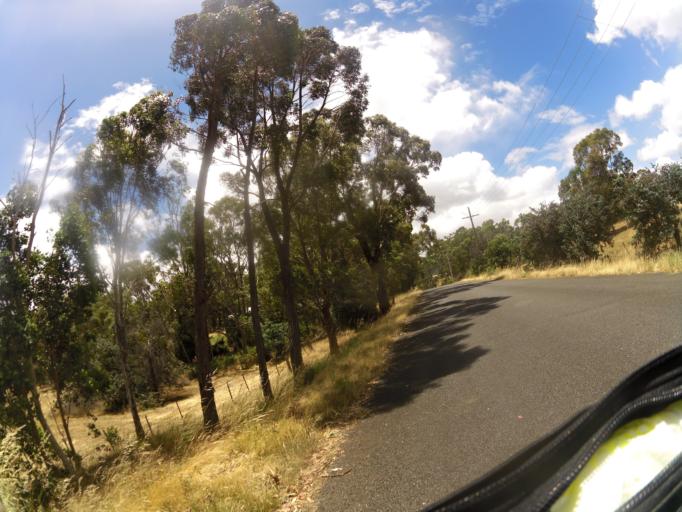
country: AU
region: Victoria
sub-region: Mount Alexander
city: Castlemaine
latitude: -37.0209
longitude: 144.2498
